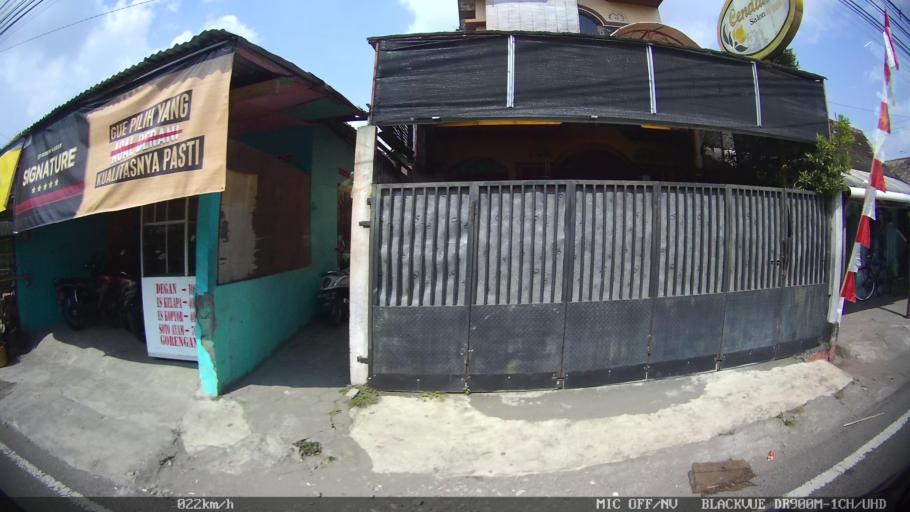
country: ID
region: Daerah Istimewa Yogyakarta
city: Yogyakarta
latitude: -7.8220
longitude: 110.3905
